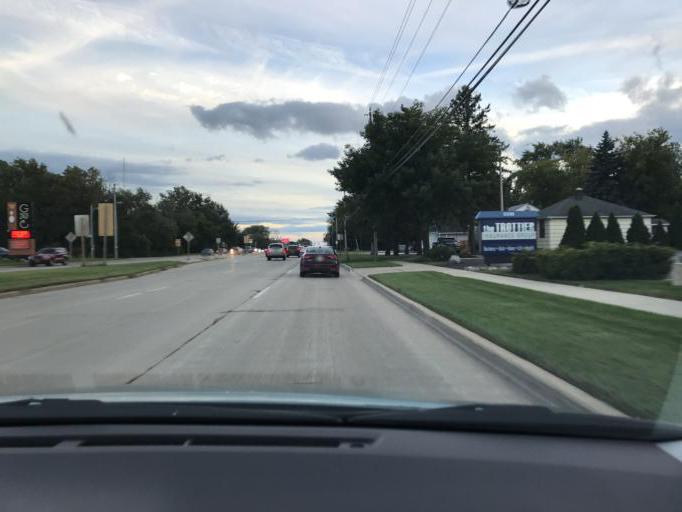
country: US
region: Wisconsin
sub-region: Kenosha County
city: Somers
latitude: 42.5875
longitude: -87.8828
